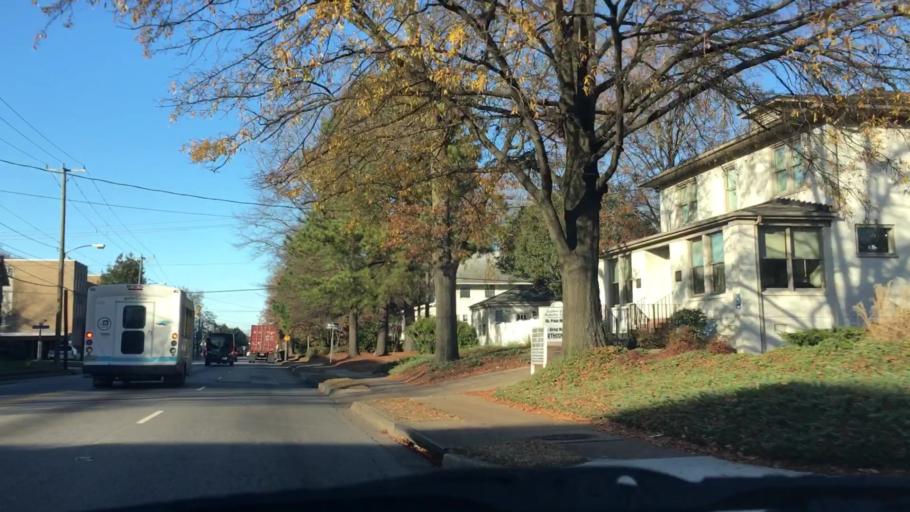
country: US
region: Virginia
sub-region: City of Norfolk
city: Norfolk
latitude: 36.8705
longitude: -76.3010
